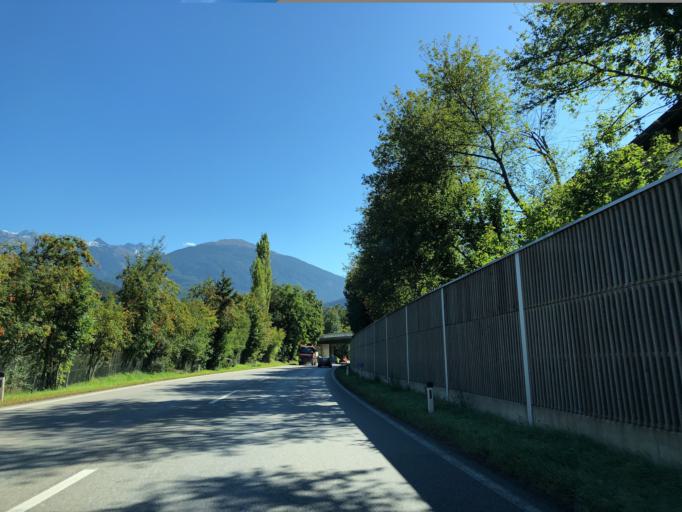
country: AT
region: Tyrol
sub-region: Politischer Bezirk Imst
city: Imst
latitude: 47.2384
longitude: 10.7442
